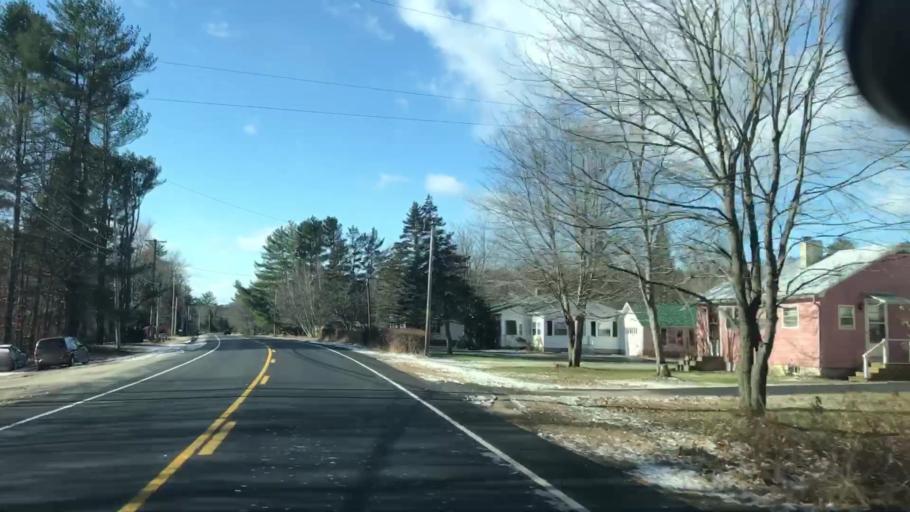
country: US
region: Maine
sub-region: Oxford County
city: Porter
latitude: 43.8047
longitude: -70.8974
